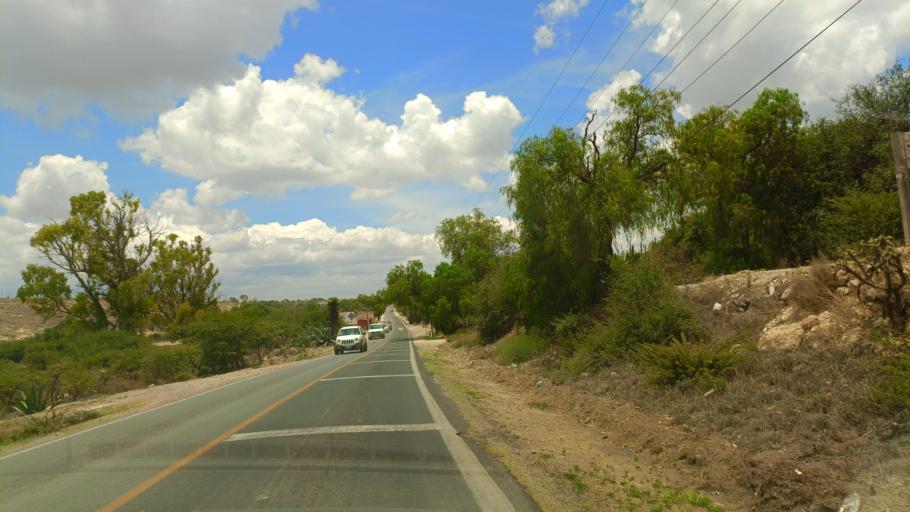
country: MX
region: Guanajuato
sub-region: San Luis de la Paz
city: San Ignacio
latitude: 21.2320
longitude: -100.4900
